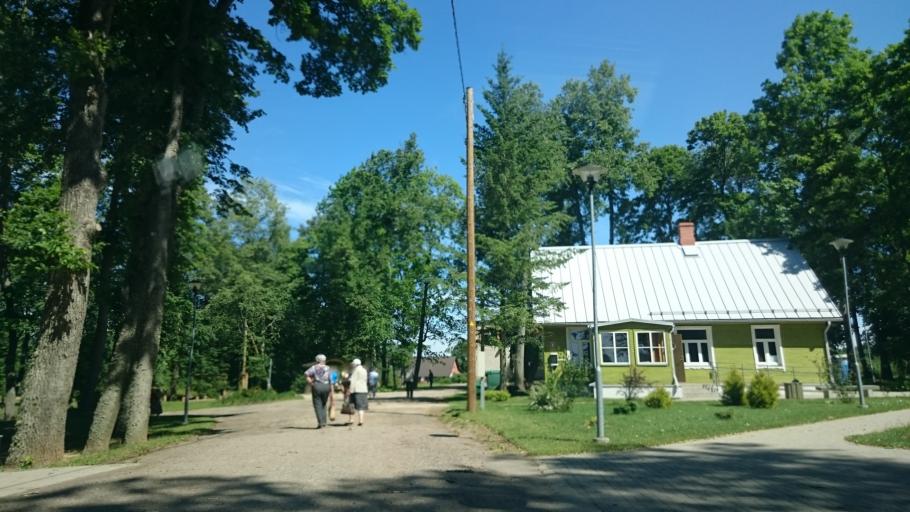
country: LV
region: Cibla
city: Cibla
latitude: 56.5933
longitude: 27.9901
